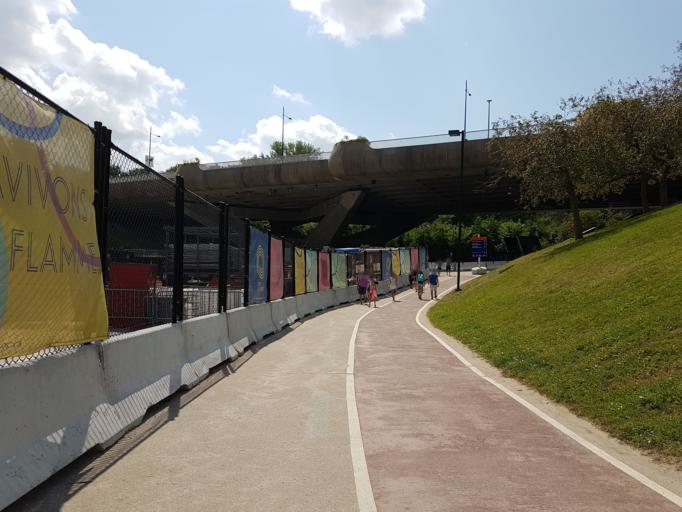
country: CA
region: Quebec
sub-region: Monteregie
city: Longueuil
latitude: 45.5601
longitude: -73.5533
